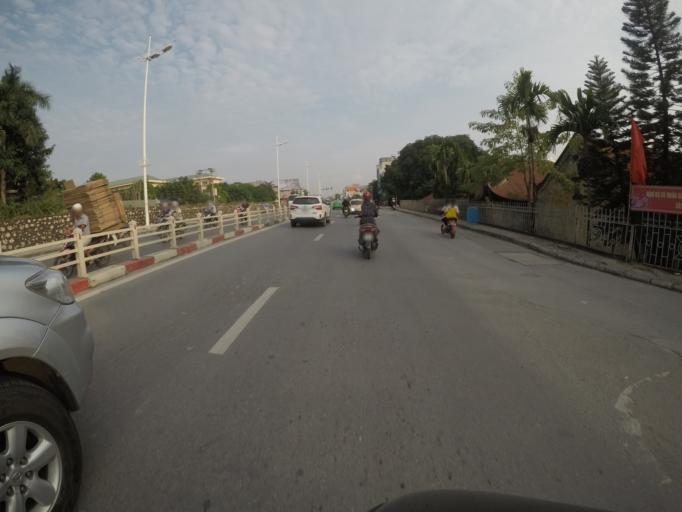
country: VN
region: Ha Noi
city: Tay Ho
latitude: 21.0765
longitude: 105.8215
